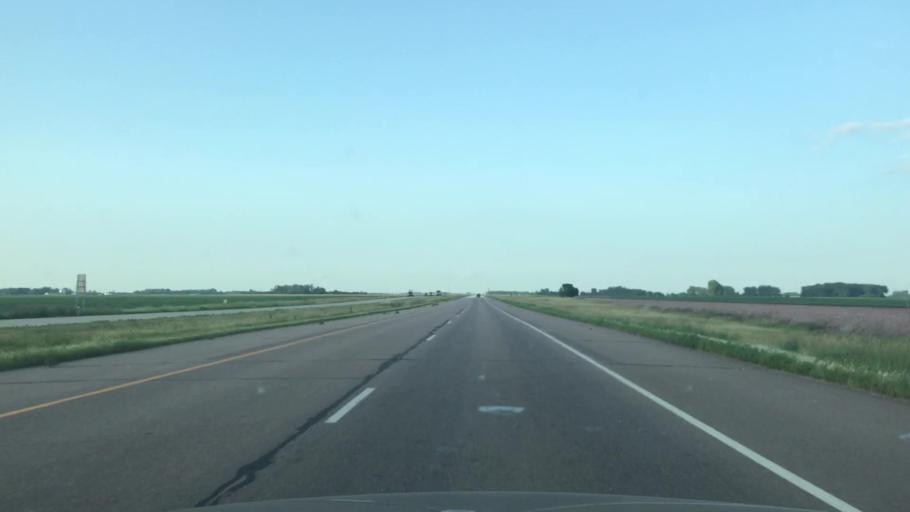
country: US
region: Minnesota
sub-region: Nobles County
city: Worthington
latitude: 43.7342
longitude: -95.4167
